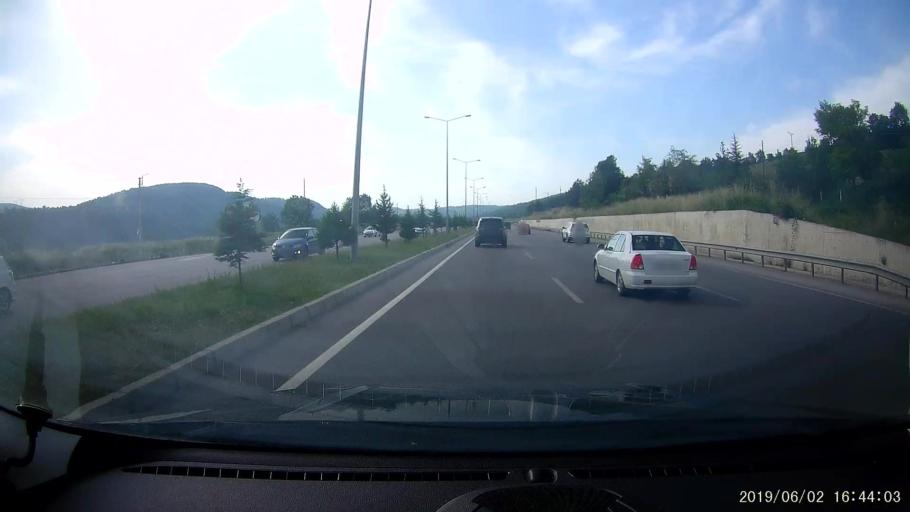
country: TR
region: Samsun
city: Kavak
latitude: 41.1444
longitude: 36.1164
